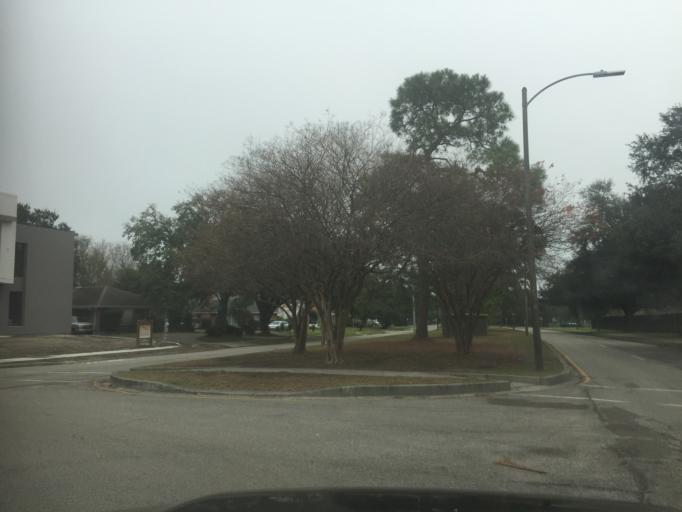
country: US
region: Louisiana
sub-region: Orleans Parish
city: New Orleans
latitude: 30.0187
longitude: -90.0899
